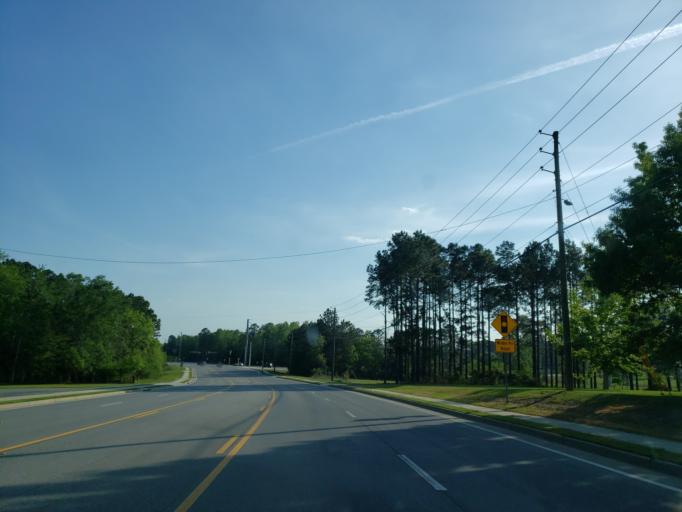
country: US
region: Georgia
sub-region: Tift County
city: Tifton
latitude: 31.4708
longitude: -83.5454
